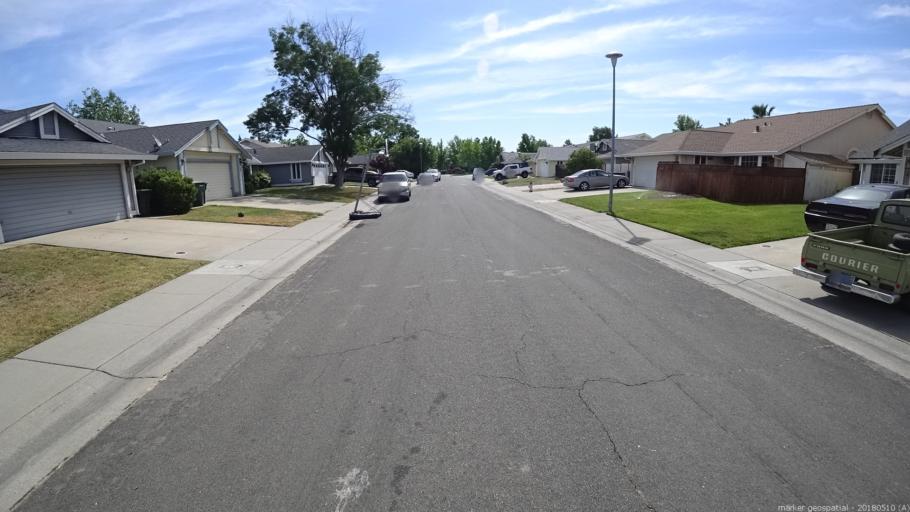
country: US
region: California
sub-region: Sacramento County
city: Rio Linda
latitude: 38.6561
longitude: -121.4610
